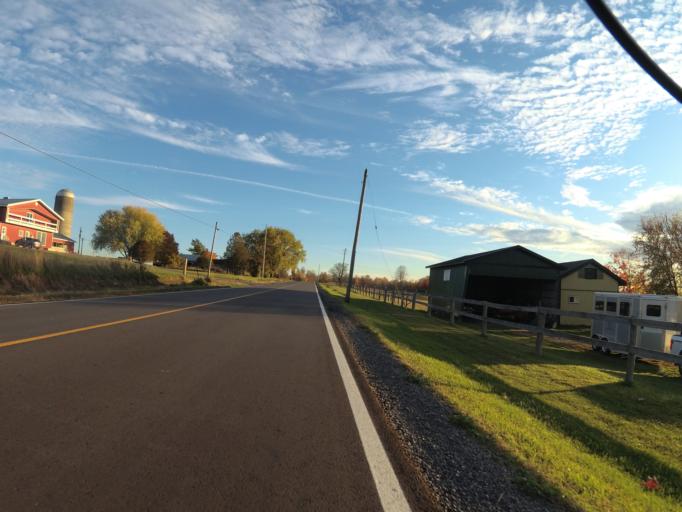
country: CA
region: Ontario
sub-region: Lanark County
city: Smiths Falls
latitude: 44.9550
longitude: -75.8137
